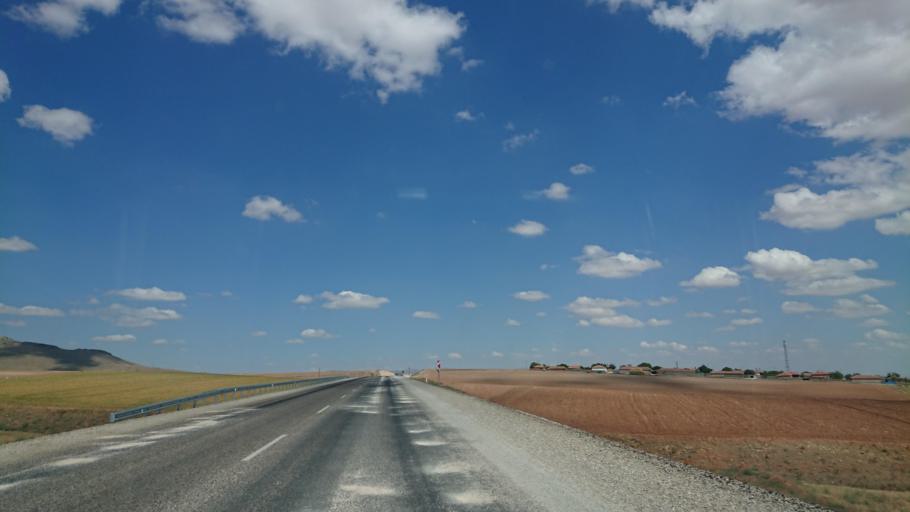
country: TR
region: Kirsehir
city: Kirsehir
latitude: 39.1237
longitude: 33.9796
